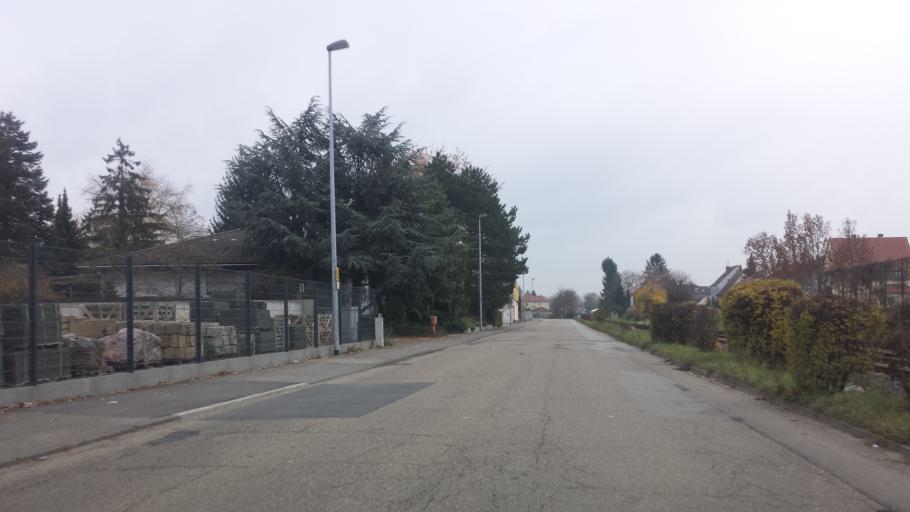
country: DE
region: Hesse
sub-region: Regierungsbezirk Darmstadt
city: Burstadt
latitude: 49.6456
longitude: 8.4637
